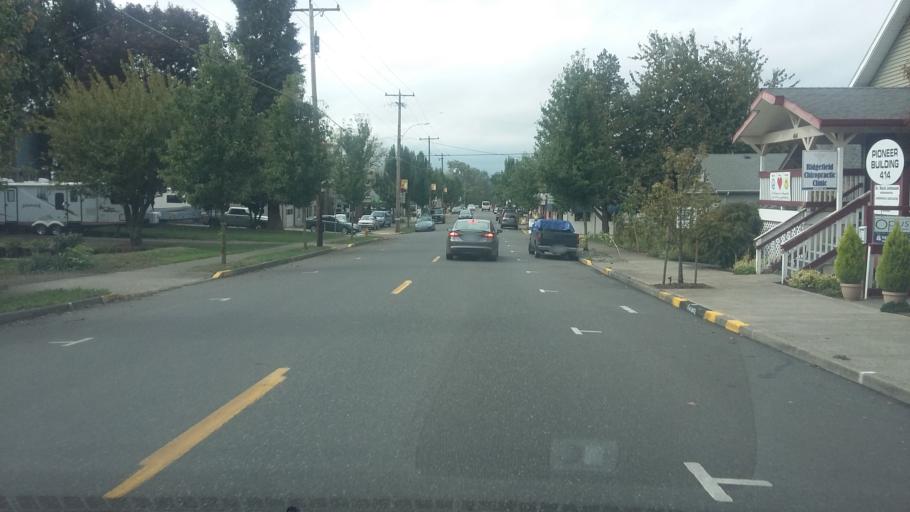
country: US
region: Washington
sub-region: Clark County
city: Ridgefield
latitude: 45.8154
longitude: -122.7430
